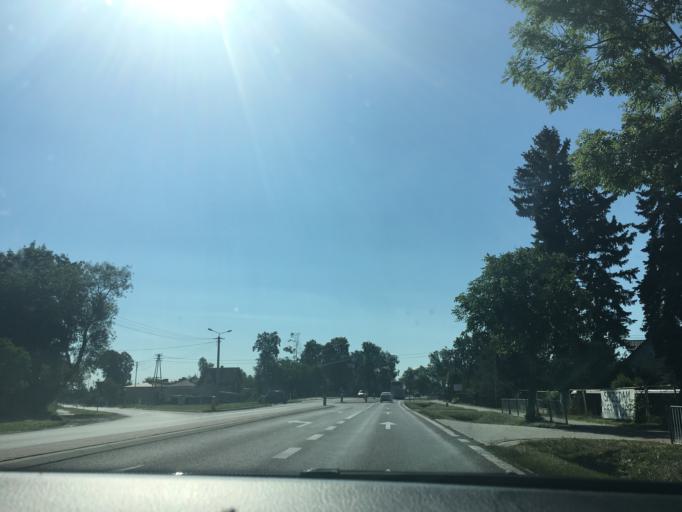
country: PL
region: Lublin Voivodeship
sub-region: Powiat lubartowski
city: Serniki
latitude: 51.4277
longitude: 22.6350
